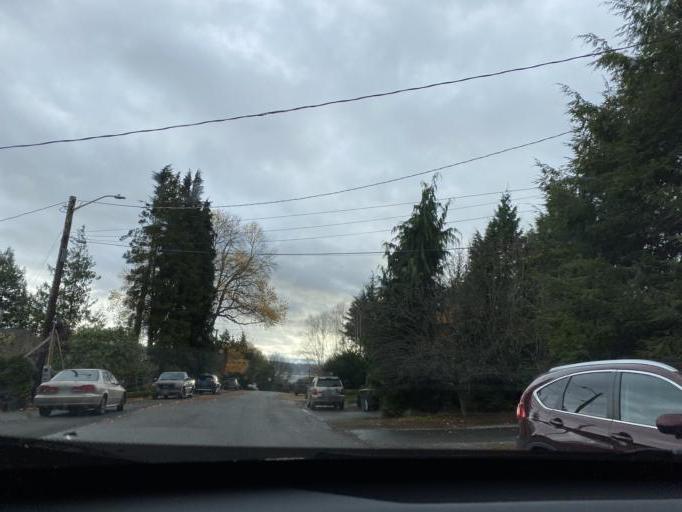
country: US
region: Washington
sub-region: King County
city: Seattle
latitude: 47.6340
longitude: -122.3902
